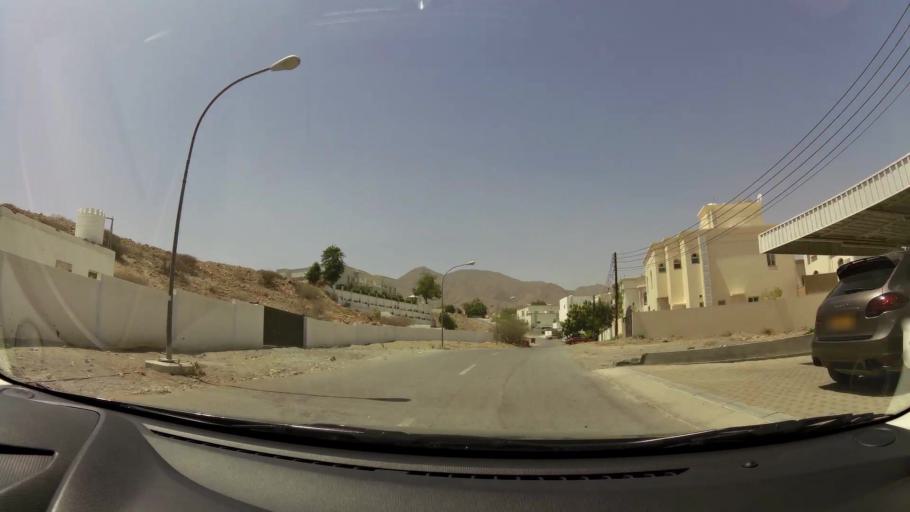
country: OM
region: Muhafazat Masqat
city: Bawshar
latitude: 23.5884
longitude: 58.4500
